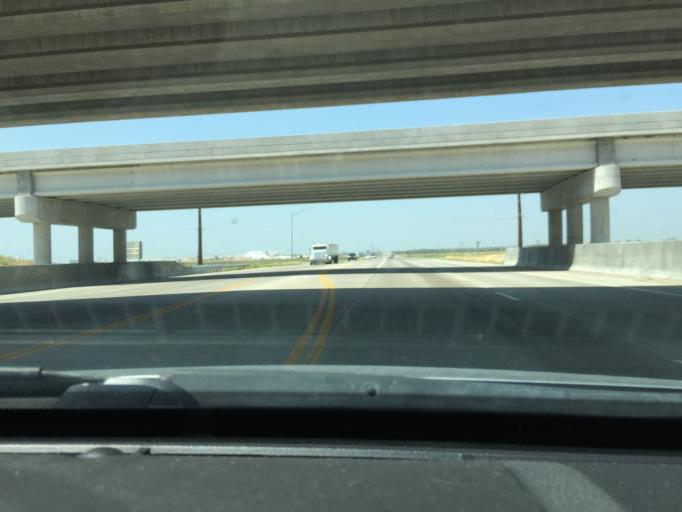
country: US
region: Kansas
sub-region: Reno County
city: Hutchinson
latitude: 38.0284
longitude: -97.8669
